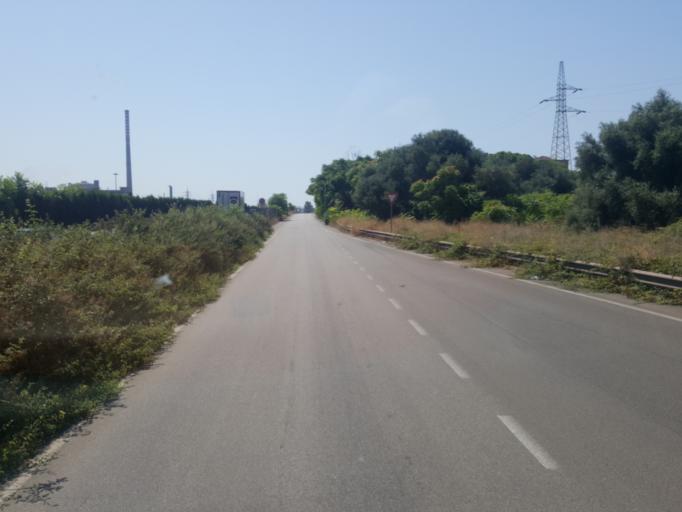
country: IT
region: Apulia
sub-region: Provincia di Taranto
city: Statte
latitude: 40.5086
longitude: 17.1935
